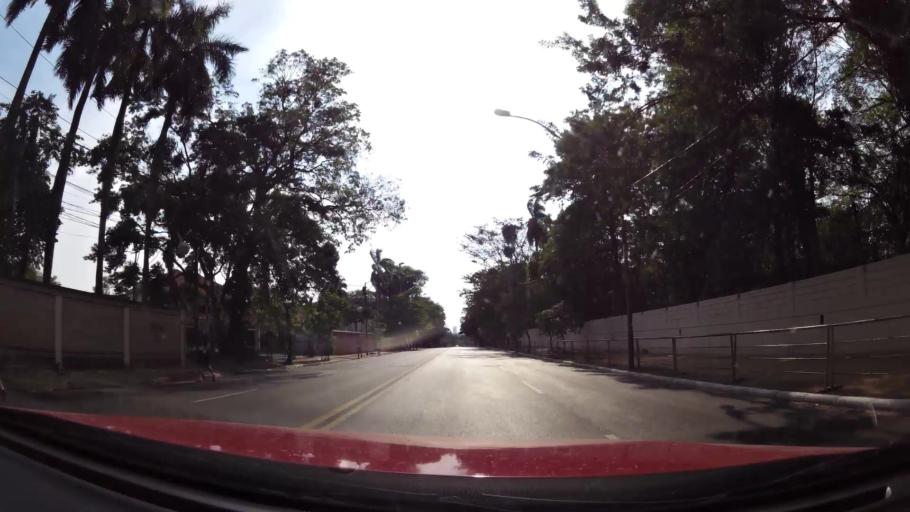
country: PY
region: Asuncion
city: Asuncion
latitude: -25.2920
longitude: -57.6007
